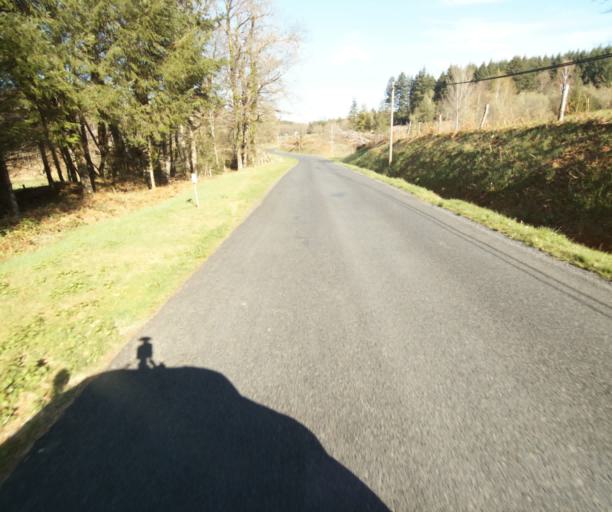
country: FR
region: Limousin
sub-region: Departement de la Correze
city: Correze
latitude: 45.2858
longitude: 1.8741
